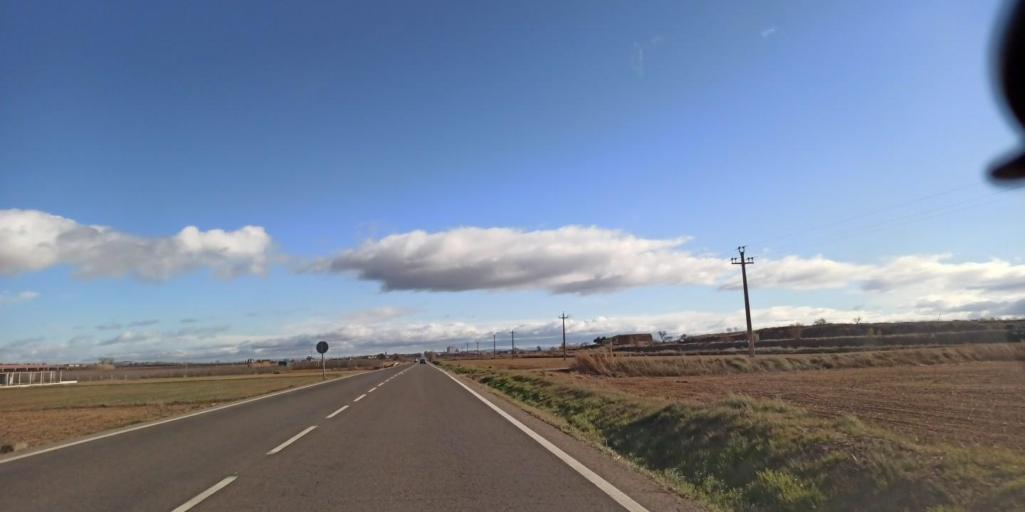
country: ES
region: Catalonia
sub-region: Provincia de Lleida
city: Bellcaire d'Urgell
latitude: 41.7708
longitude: 0.8705
